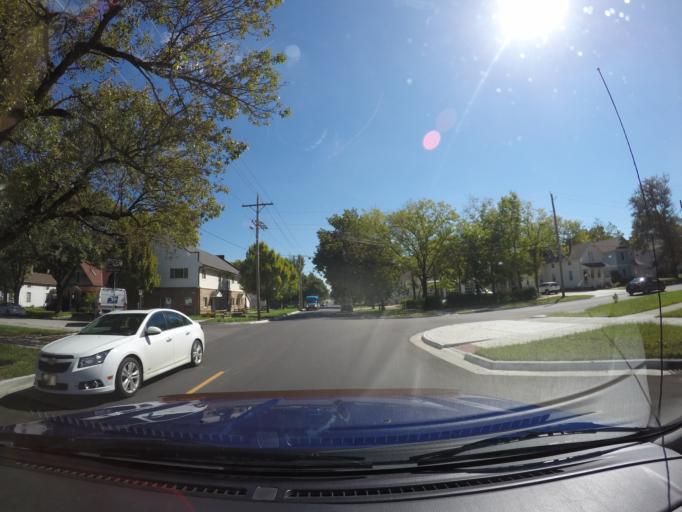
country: US
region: Kansas
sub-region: Douglas County
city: Lawrence
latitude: 38.9638
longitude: -95.2338
